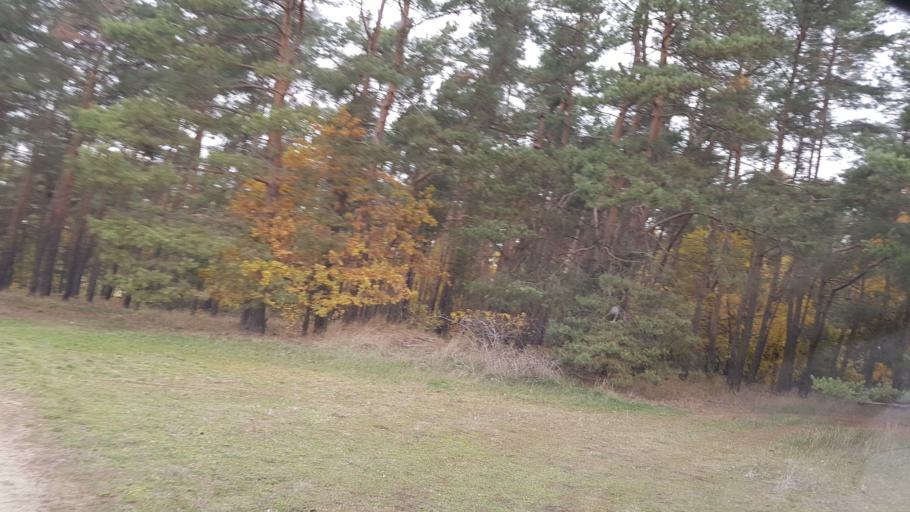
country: DE
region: Brandenburg
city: Crinitz
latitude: 51.7293
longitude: 13.7596
